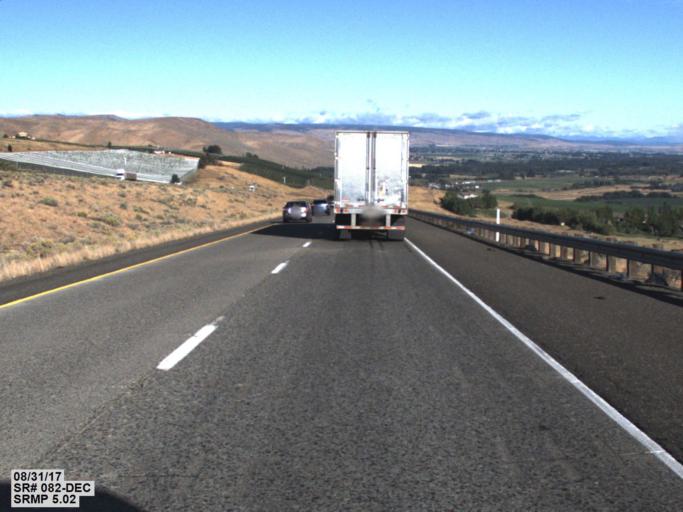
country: US
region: Washington
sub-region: Kittitas County
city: Kittitas
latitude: 46.9109
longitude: -120.4690
